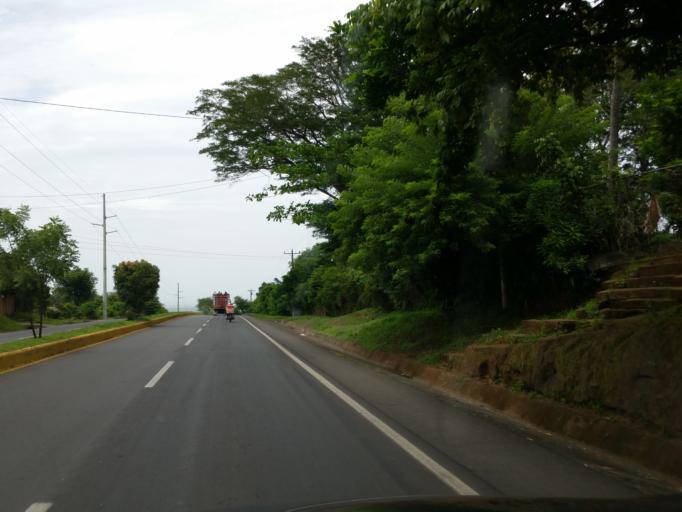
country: NI
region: Masaya
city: Masaya
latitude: 11.9763
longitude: -86.0592
